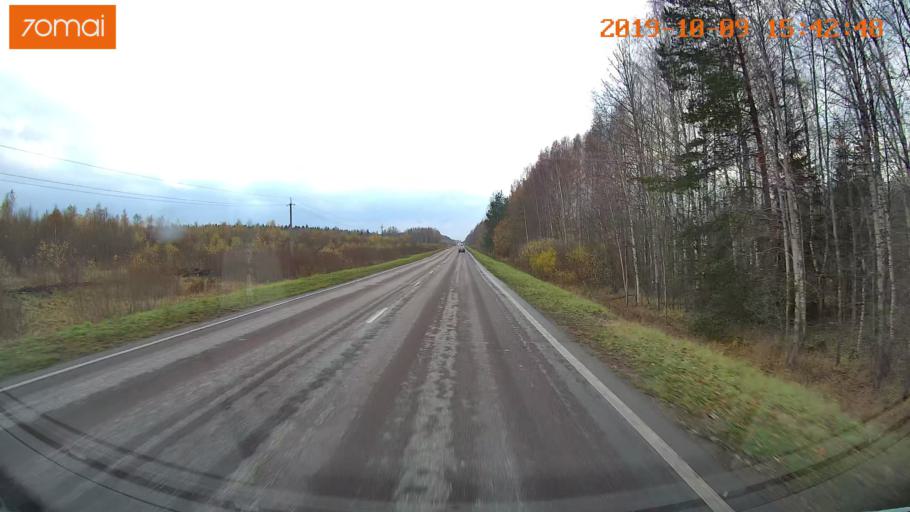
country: RU
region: Kostroma
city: Oktyabr'skiy
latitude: 57.8645
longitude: 41.1002
